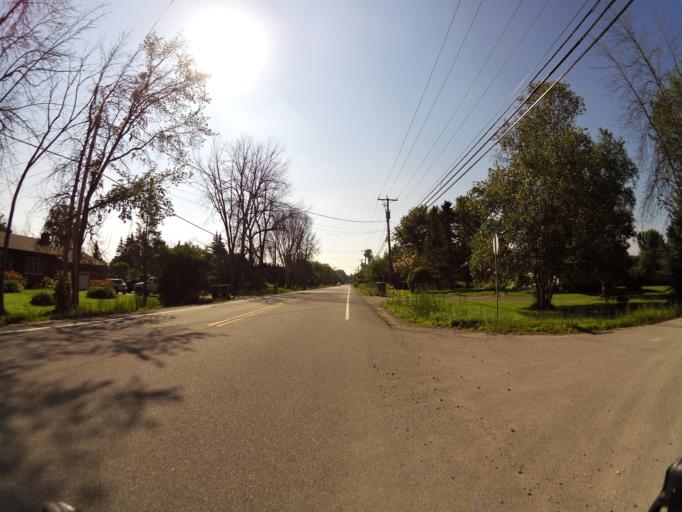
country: CA
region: Quebec
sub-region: Outaouais
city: Gatineau
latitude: 45.4945
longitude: -75.7737
